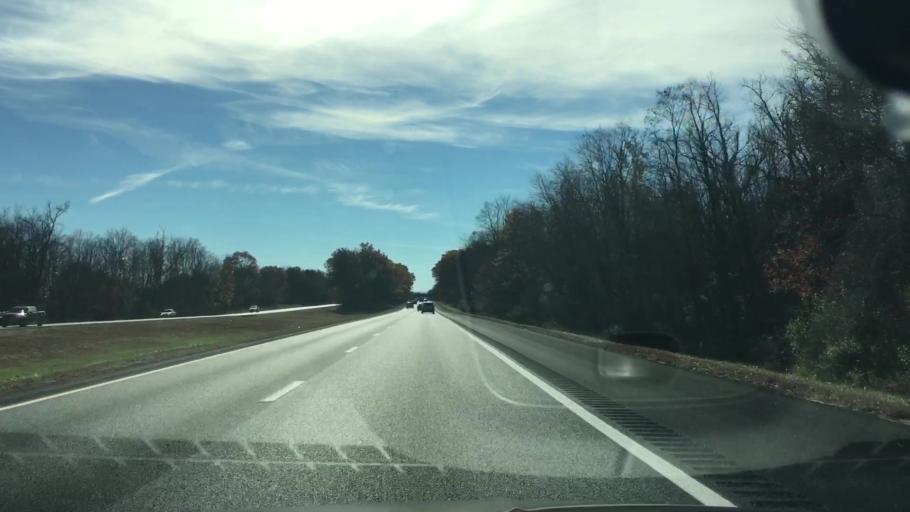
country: US
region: Massachusetts
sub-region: Franklin County
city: Whately
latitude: 42.4064
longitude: -72.6272
